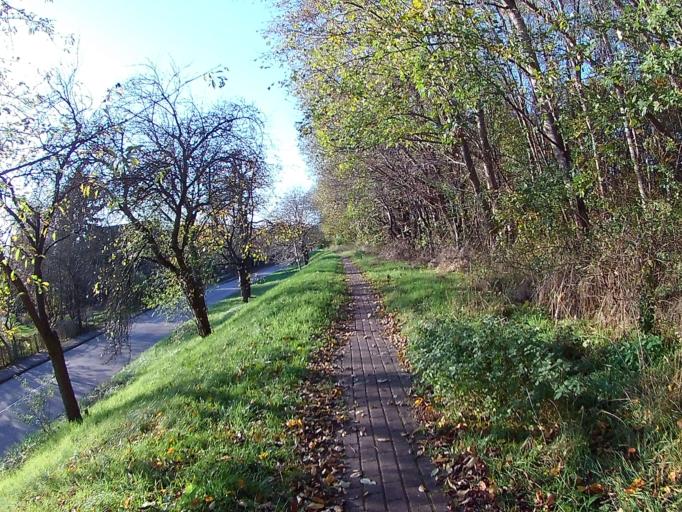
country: DE
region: Hamburg
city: Altona
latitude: 53.4952
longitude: 9.9242
